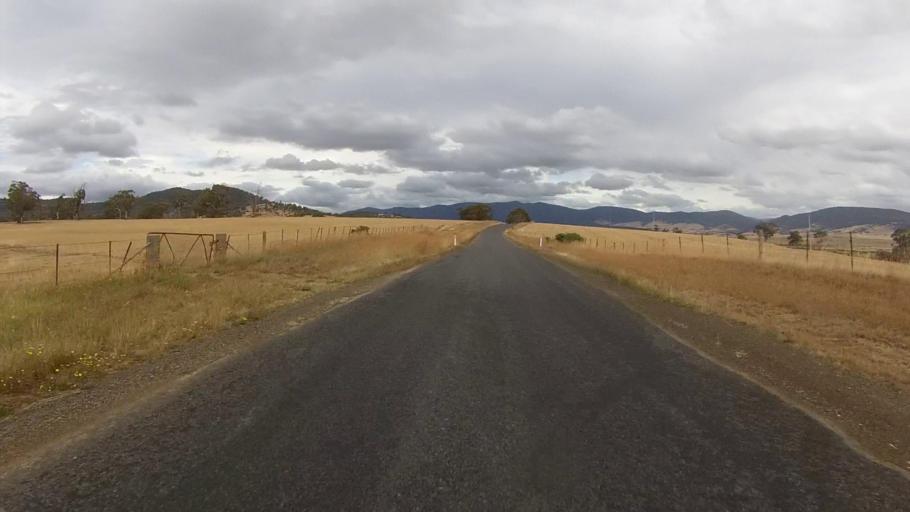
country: AU
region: Tasmania
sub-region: Northern Midlands
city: Evandale
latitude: -41.7923
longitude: 147.7432
